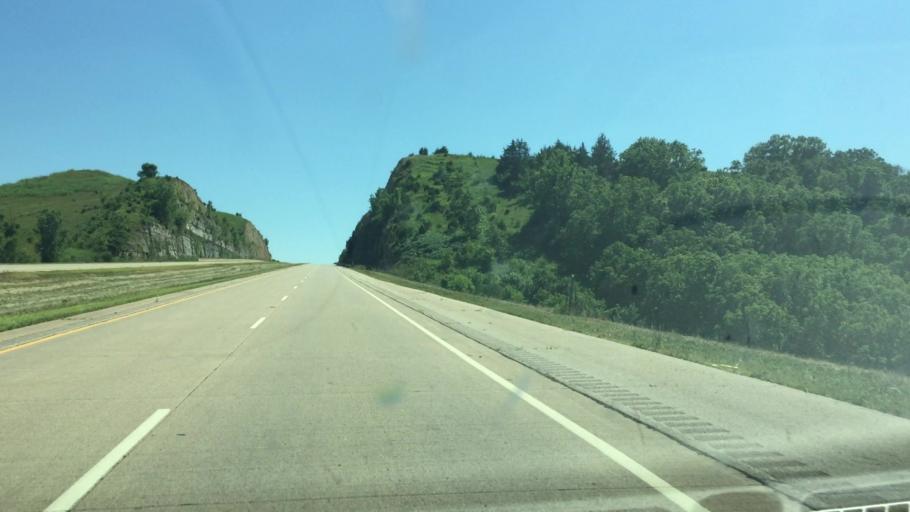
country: US
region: Wisconsin
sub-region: Grant County
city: Dickeyville
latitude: 42.6430
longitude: -90.5774
